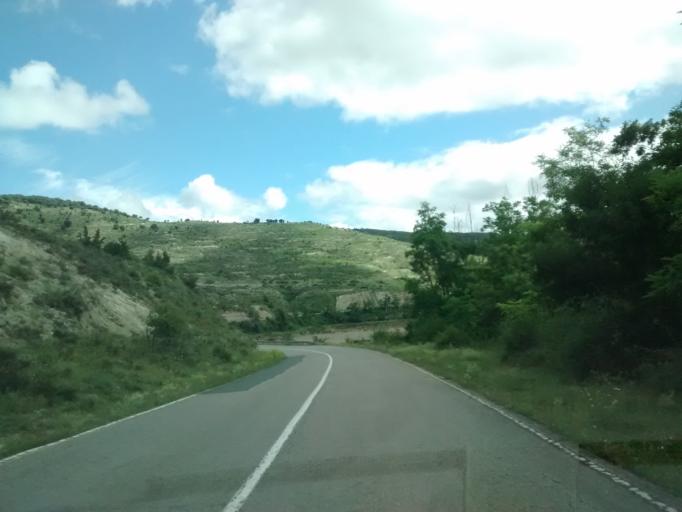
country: ES
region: La Rioja
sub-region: Provincia de La Rioja
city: Terroba
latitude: 42.2528
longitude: -2.4551
